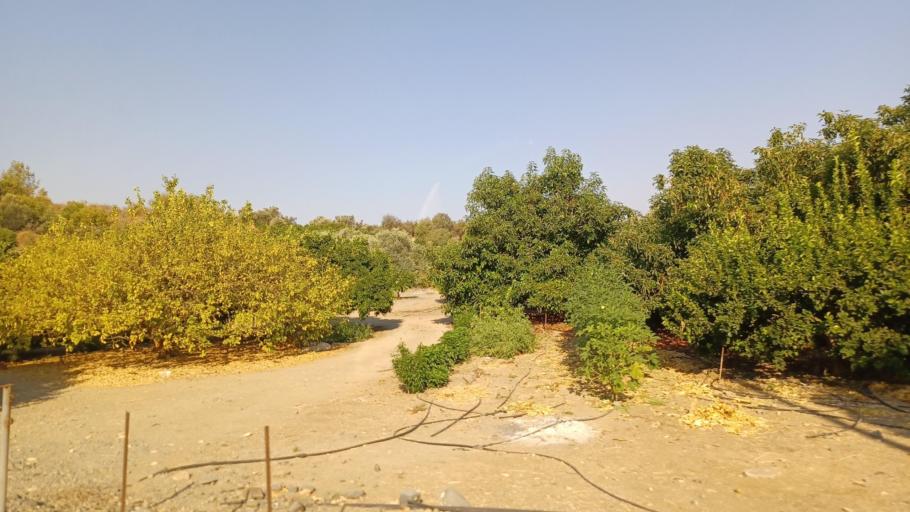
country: CY
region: Pafos
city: Polis
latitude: 35.0579
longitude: 32.4798
